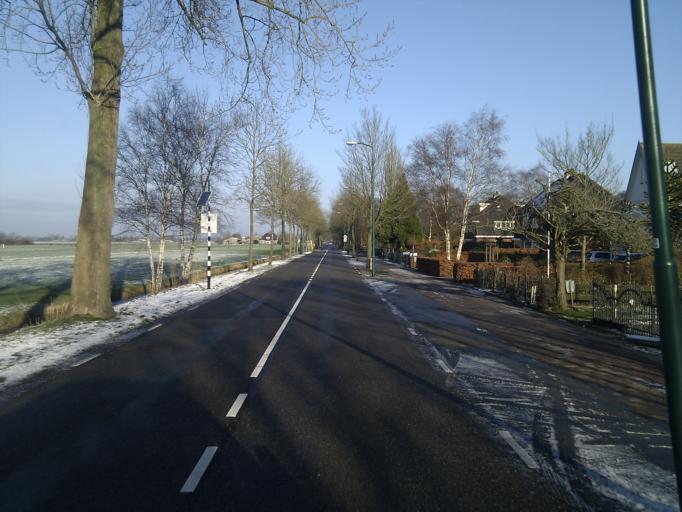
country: NL
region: Utrecht
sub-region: Gemeente De Bilt
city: De Bilt
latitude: 52.1339
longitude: 5.1503
